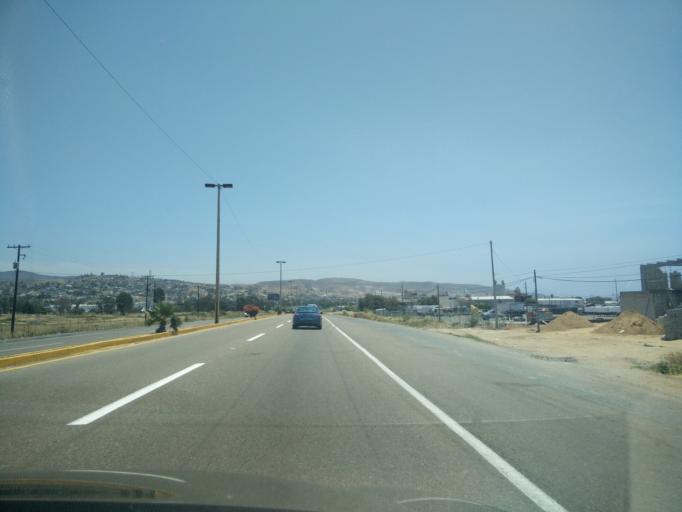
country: MX
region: Baja California
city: El Sauzal
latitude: 31.9014
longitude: -116.7125
